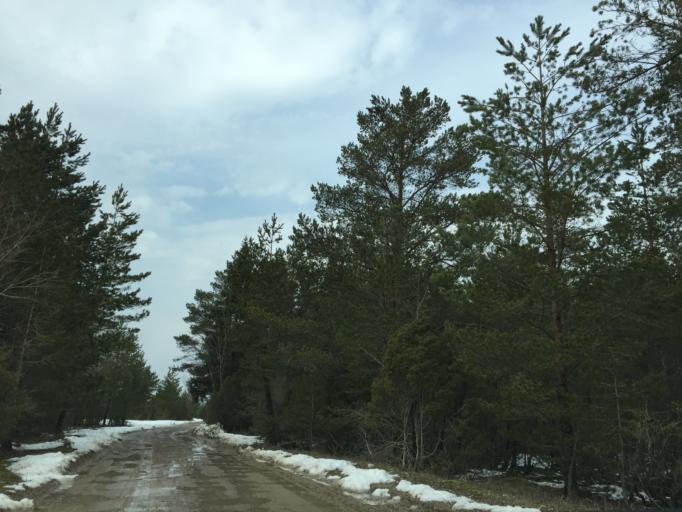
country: EE
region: Saare
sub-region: Kuressaare linn
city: Kuressaare
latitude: 58.4326
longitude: 22.1431
